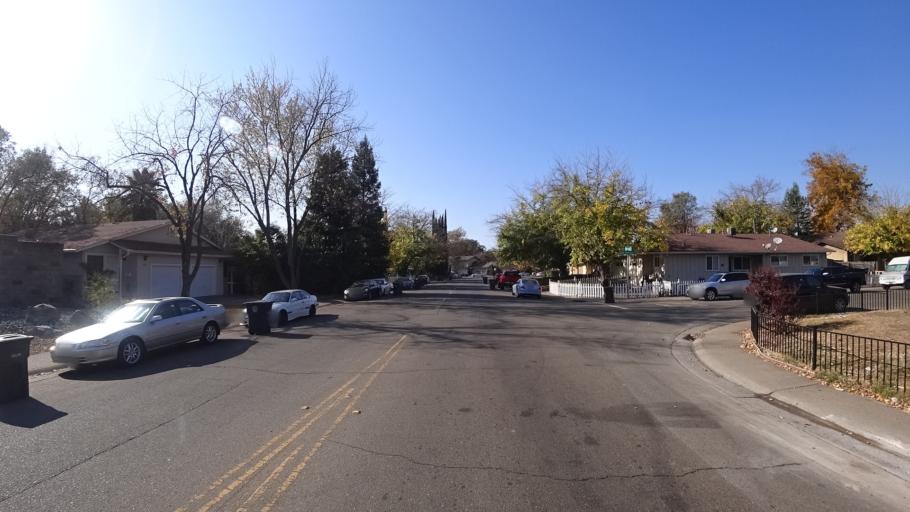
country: US
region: California
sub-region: Sacramento County
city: Citrus Heights
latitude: 38.6823
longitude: -121.2812
